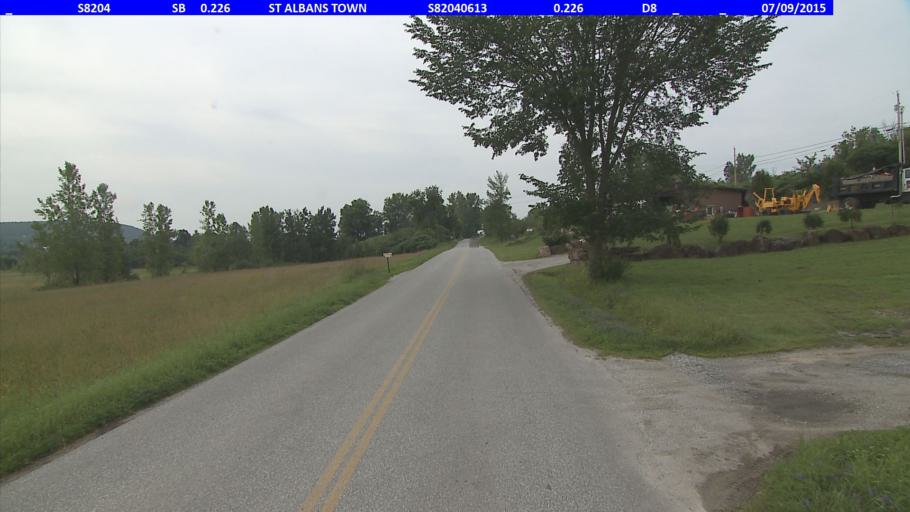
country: US
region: Vermont
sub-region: Franklin County
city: Saint Albans
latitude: 44.8060
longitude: -73.1117
